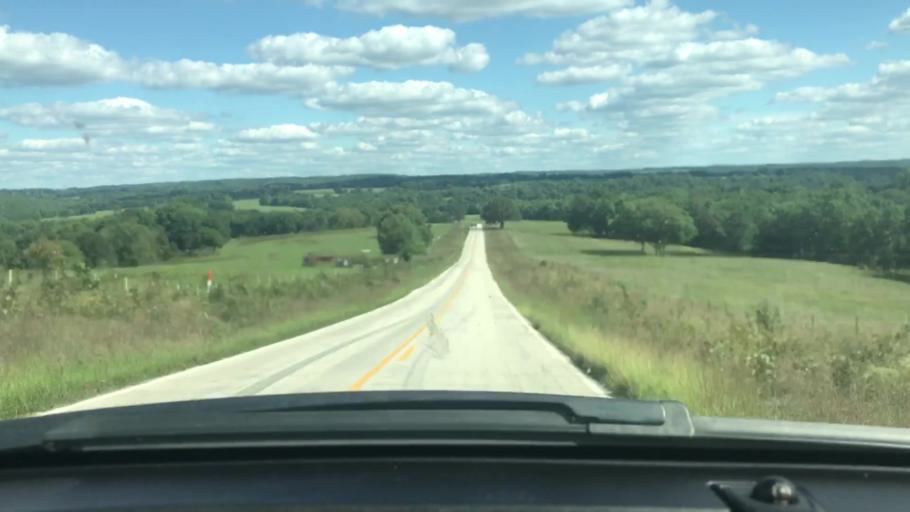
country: US
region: Missouri
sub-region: Wright County
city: Hartville
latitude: 37.3753
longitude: -92.4050
